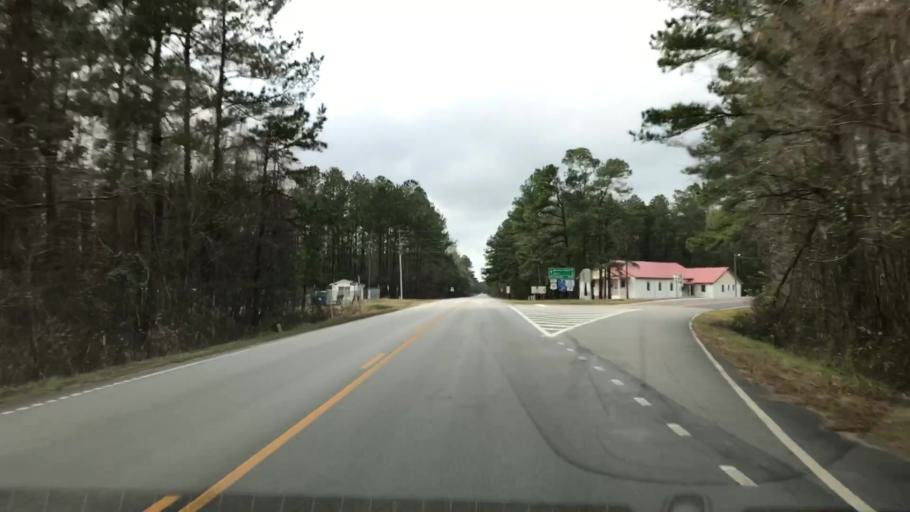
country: US
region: South Carolina
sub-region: Berkeley County
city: Saint Stephen
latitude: 33.2865
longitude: -79.7564
